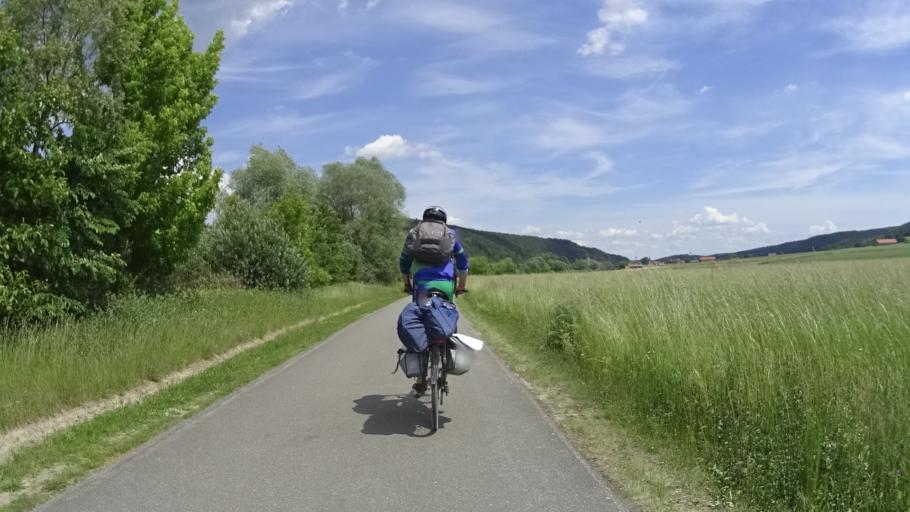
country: DE
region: Bavaria
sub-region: Lower Bavaria
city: Bad Abbach
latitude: 48.9598
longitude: 11.9913
